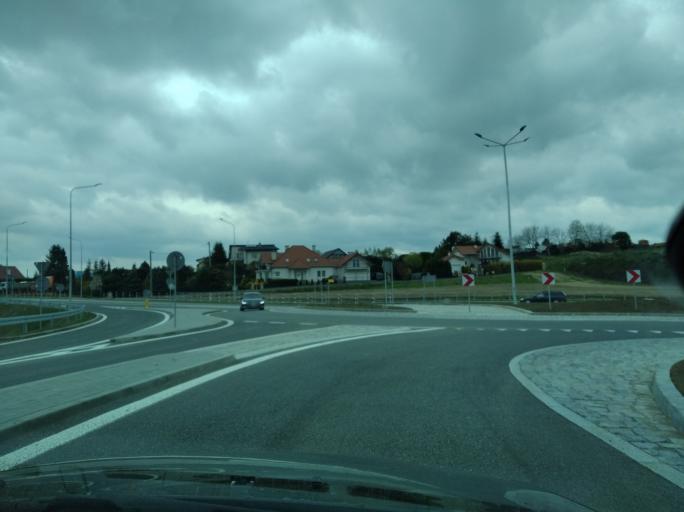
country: PL
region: Subcarpathian Voivodeship
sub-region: Powiat sanocki
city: Sanok
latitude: 49.5692
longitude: 22.1500
